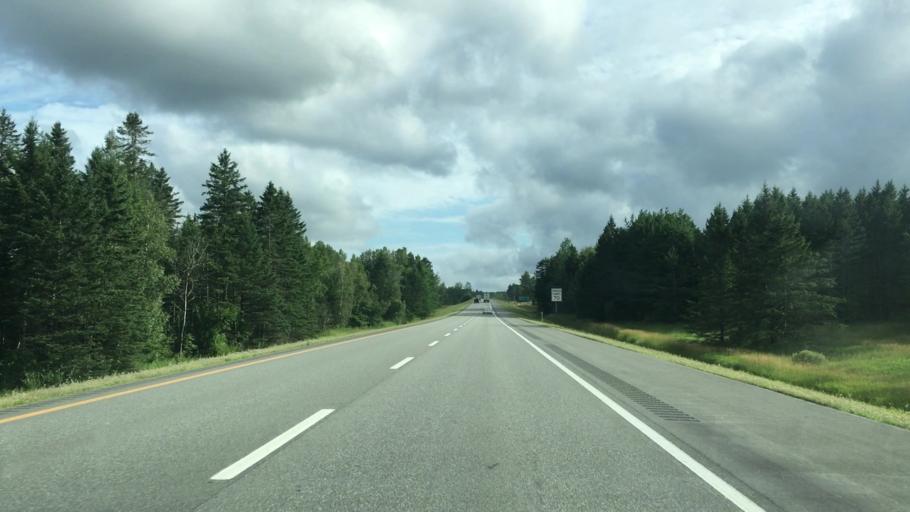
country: US
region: Maine
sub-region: Somerset County
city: Pittsfield
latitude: 44.7759
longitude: -69.4087
